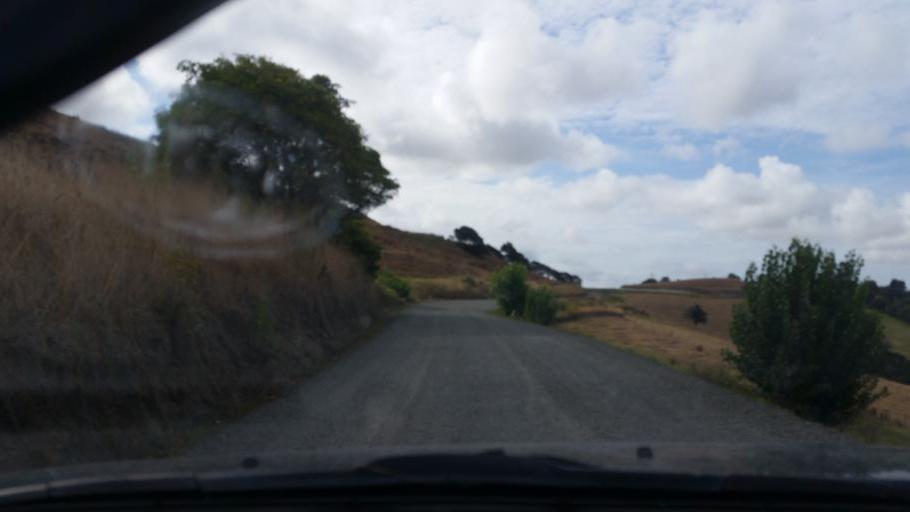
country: NZ
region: Northland
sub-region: Kaipara District
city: Dargaville
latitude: -35.9809
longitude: 173.9546
